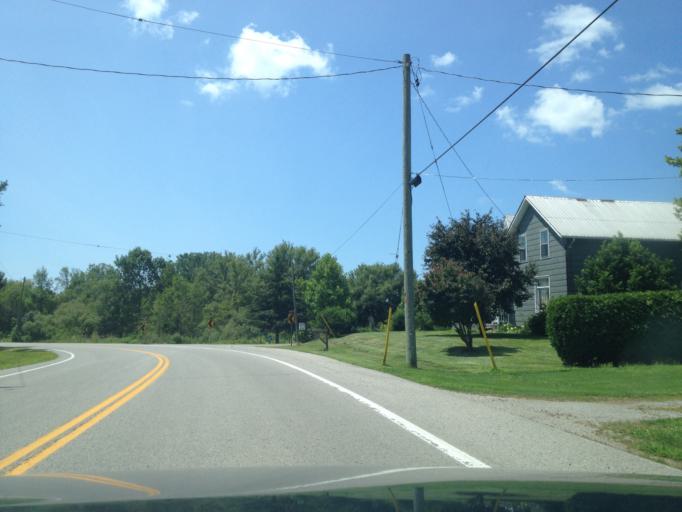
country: CA
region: Ontario
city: Norfolk County
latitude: 42.5981
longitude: -80.4842
